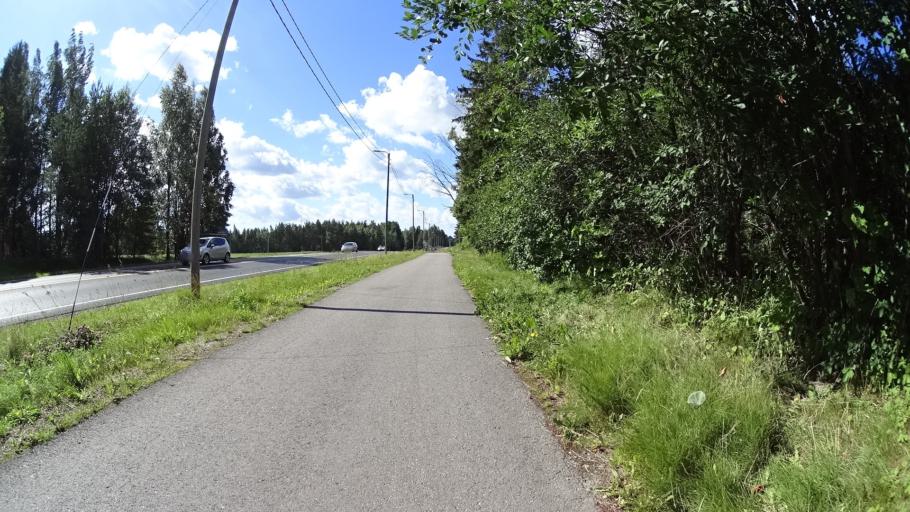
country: FI
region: Uusimaa
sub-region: Helsinki
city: Jaervenpaeae
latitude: 60.4388
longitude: 25.0699
